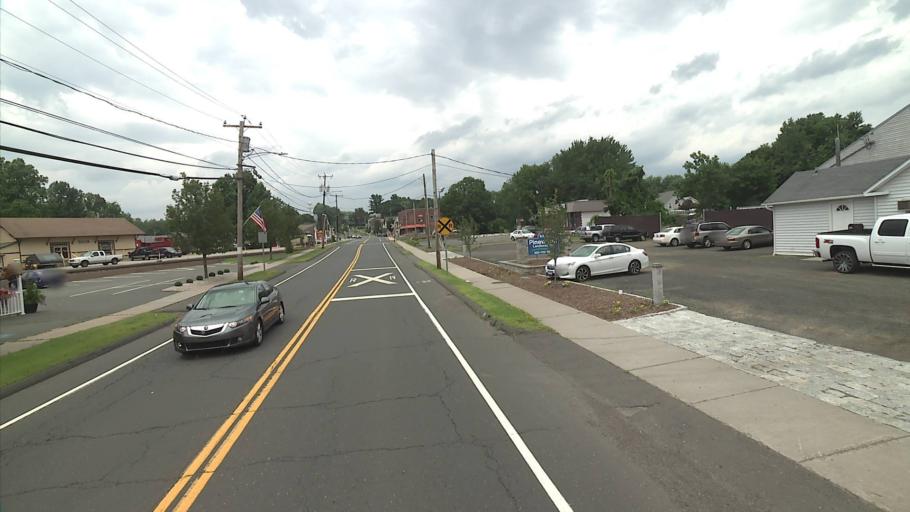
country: US
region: Connecticut
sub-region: Middlesex County
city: Cromwell
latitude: 41.5935
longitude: -72.6459
